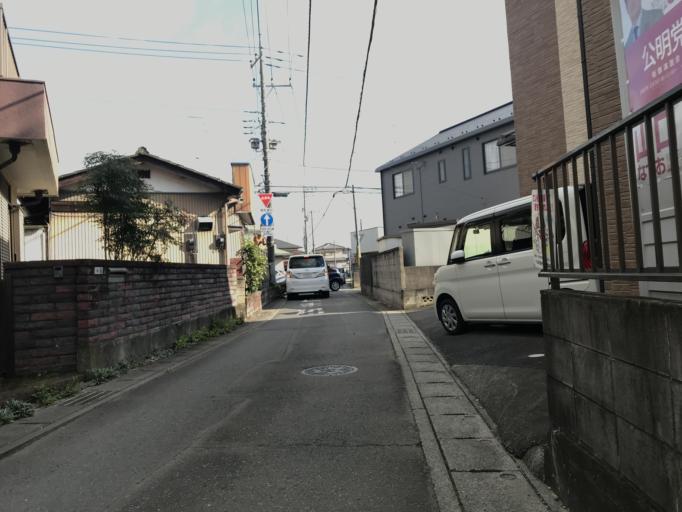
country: JP
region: Tochigi
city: Oyama
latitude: 36.2709
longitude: 139.7664
